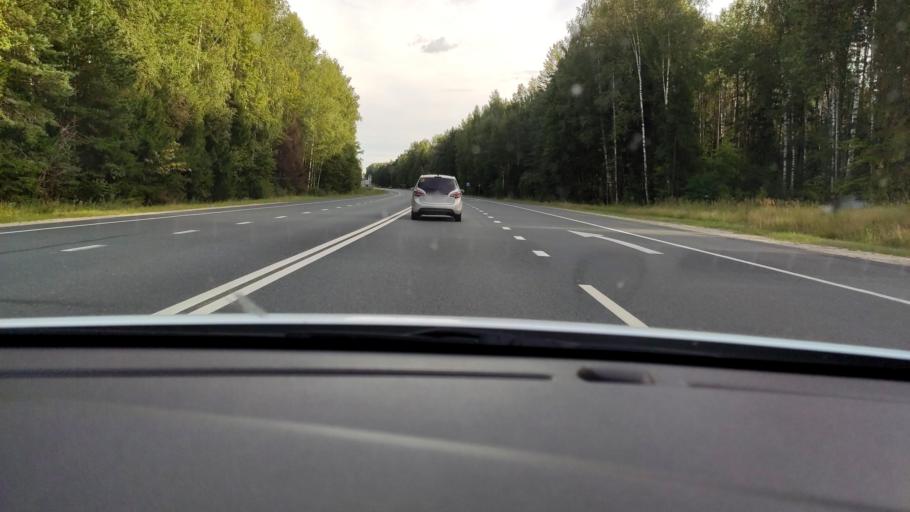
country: RU
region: Mariy-El
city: Suslonger
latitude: 56.2379
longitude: 48.2317
